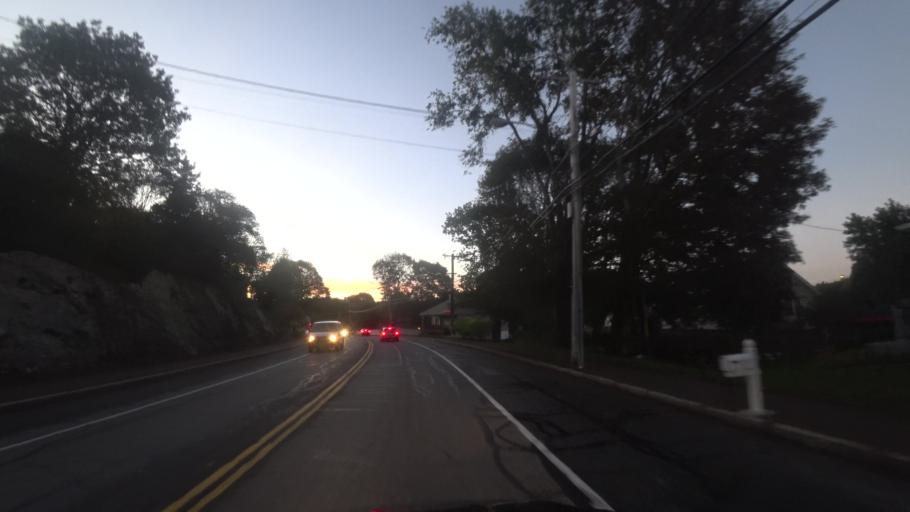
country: US
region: Massachusetts
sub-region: Essex County
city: Saugus
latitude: 42.4741
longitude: -71.0383
